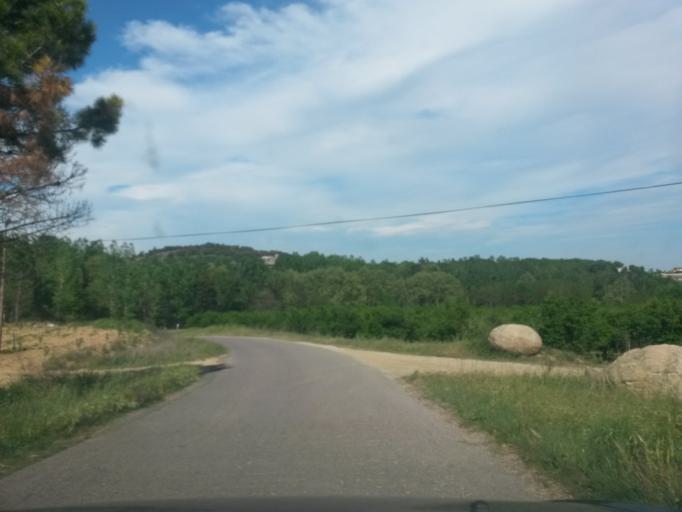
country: ES
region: Catalonia
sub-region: Provincia de Girona
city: Vilobi d'Onyar
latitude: 41.9137
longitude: 2.7247
